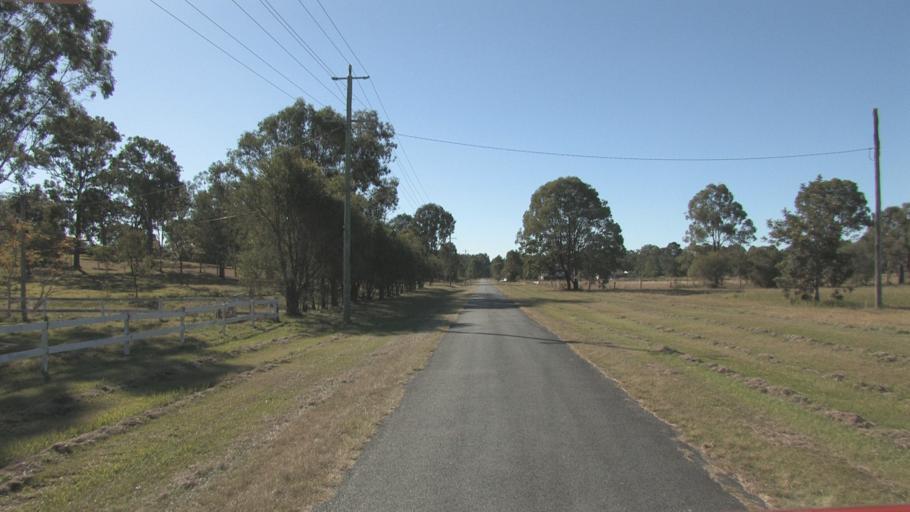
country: AU
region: Queensland
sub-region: Logan
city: North Maclean
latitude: -27.7816
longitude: 153.0189
